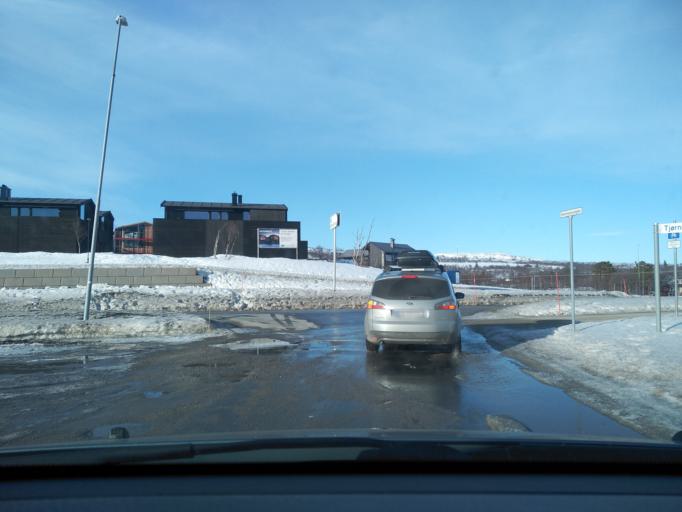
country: NO
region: Aust-Agder
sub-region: Bykle
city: Hovden
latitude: 59.5657
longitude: 7.3633
